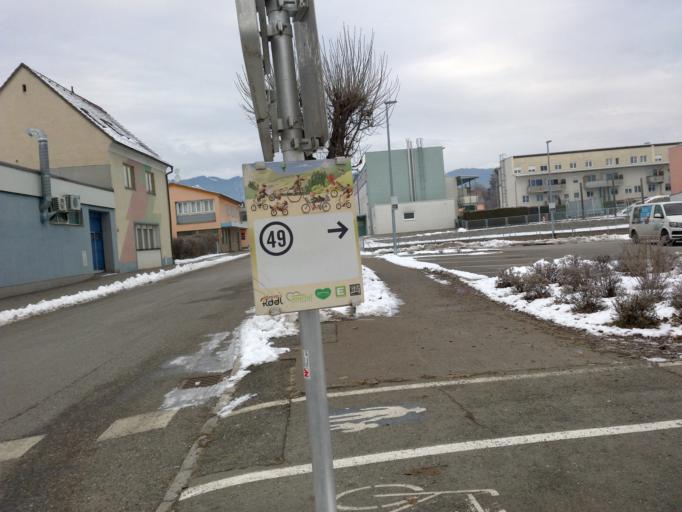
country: AT
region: Styria
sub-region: Politischer Bezirk Murtal
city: Zeltweg
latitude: 47.1917
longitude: 14.7541
